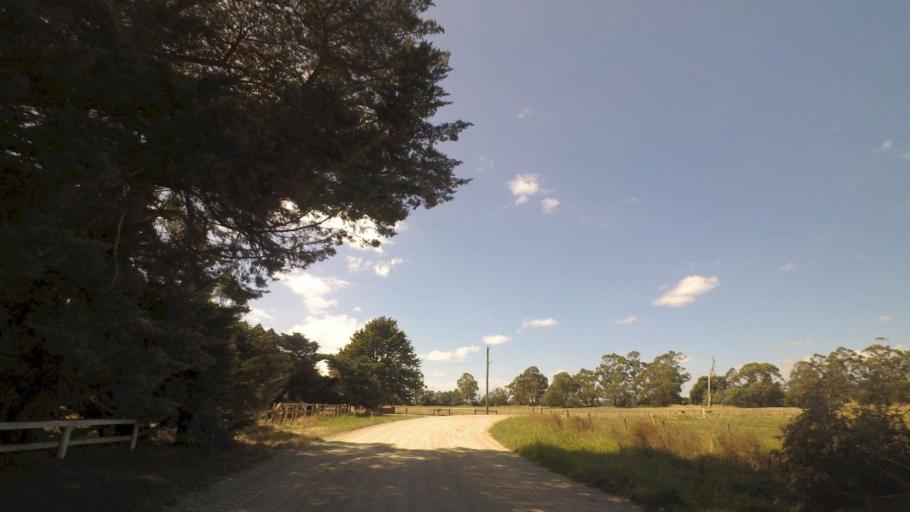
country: AU
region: Victoria
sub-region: Cardinia
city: Bunyip
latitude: -38.2730
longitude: 145.6620
